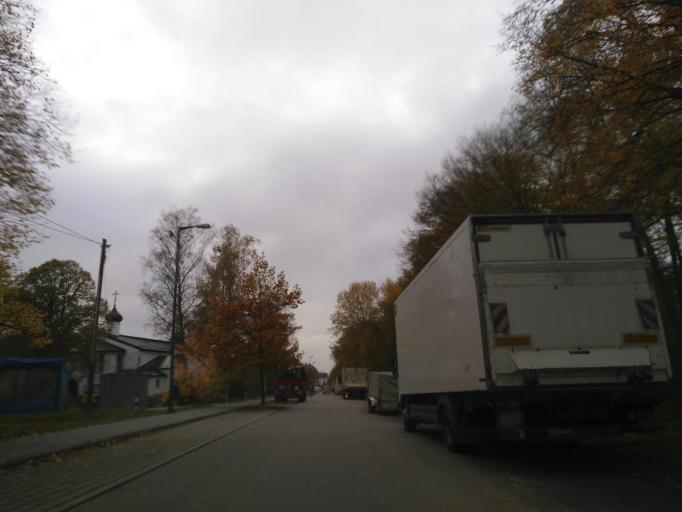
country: DE
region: Bavaria
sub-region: Upper Bavaria
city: Unterhaching
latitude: 48.0961
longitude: 11.5969
